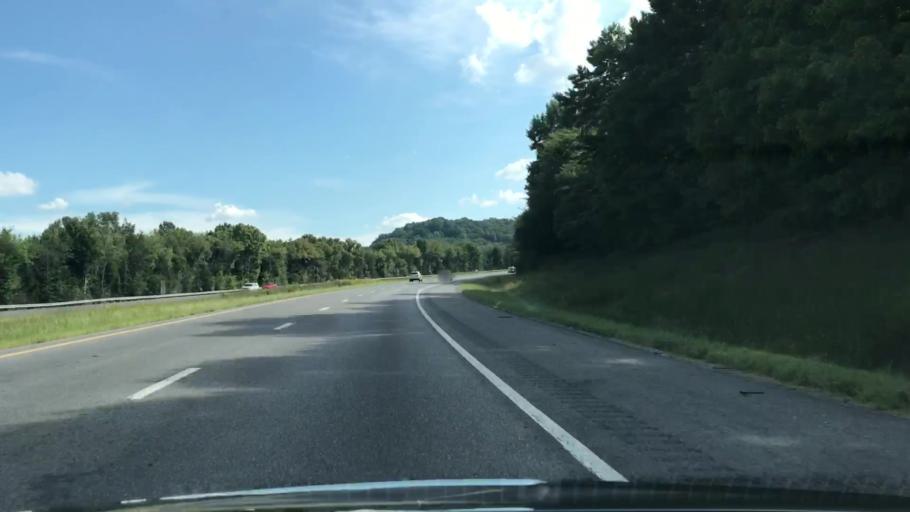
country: US
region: Tennessee
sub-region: Marshall County
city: Cornersville
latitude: 35.4168
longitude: -86.8772
